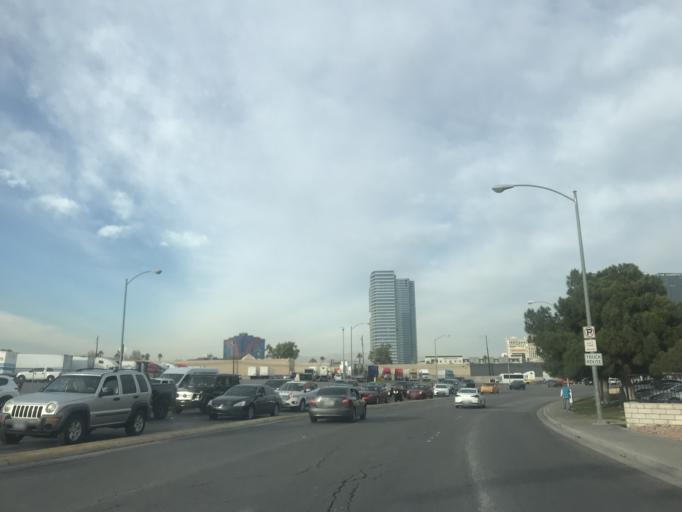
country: US
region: Nevada
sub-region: Clark County
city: Paradise
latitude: 36.1009
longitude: -115.1829
